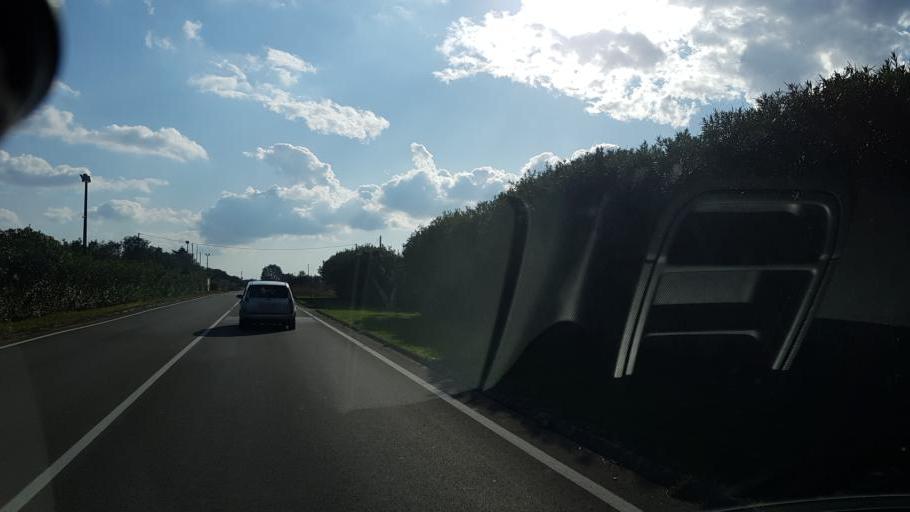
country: IT
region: Apulia
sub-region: Provincia di Lecce
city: Salice Salentino
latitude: 40.3645
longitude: 17.9675
